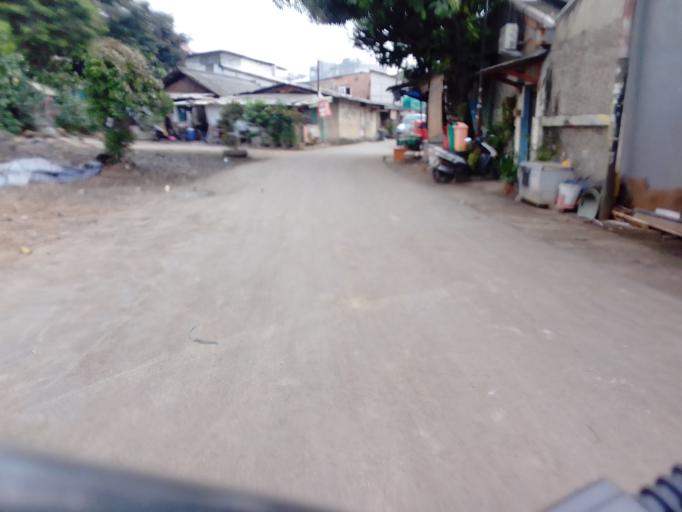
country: ID
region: Jakarta Raya
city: Jakarta
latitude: -6.2040
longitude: 106.8109
